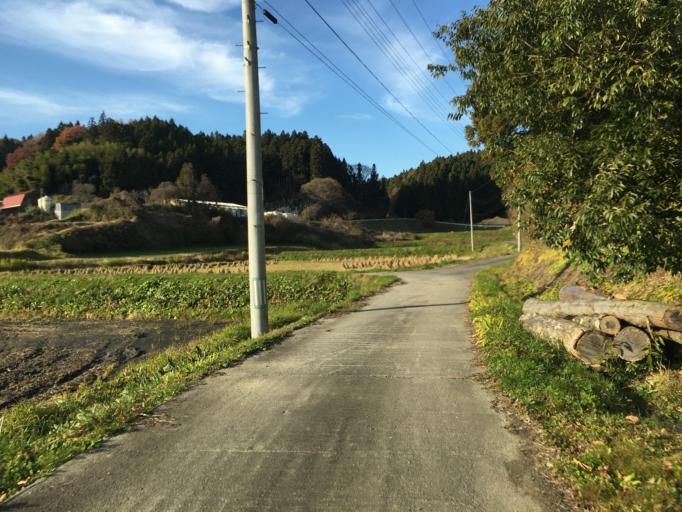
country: JP
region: Fukushima
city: Ishikawa
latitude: 37.2410
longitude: 140.5879
